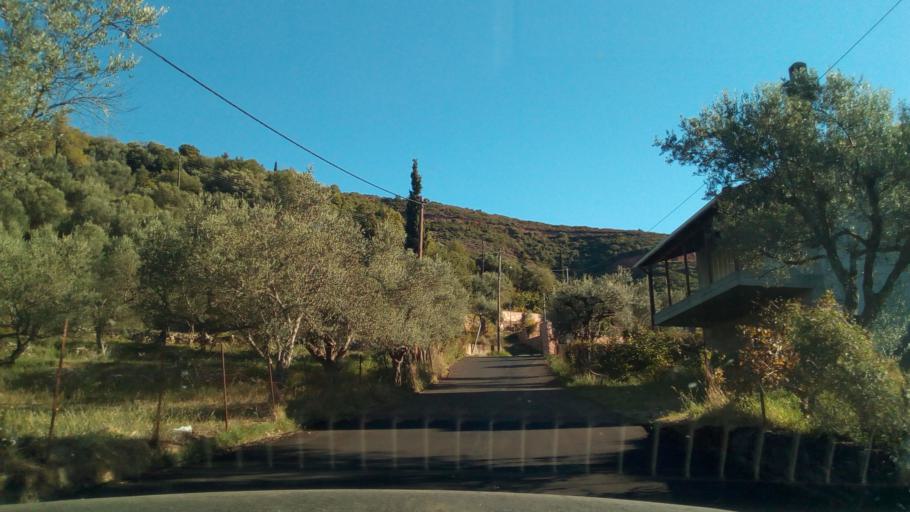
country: GR
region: West Greece
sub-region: Nomos Aitolias kai Akarnanias
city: Nafpaktos
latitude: 38.4203
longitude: 21.8447
